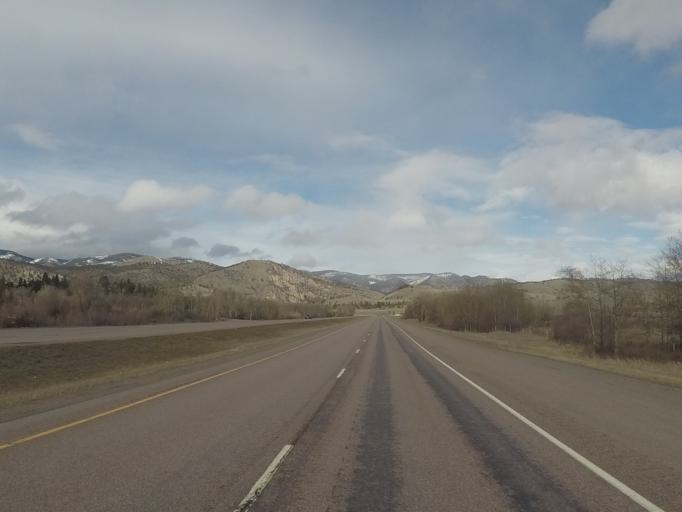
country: US
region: Montana
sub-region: Missoula County
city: Clinton
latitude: 46.6988
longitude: -113.3515
